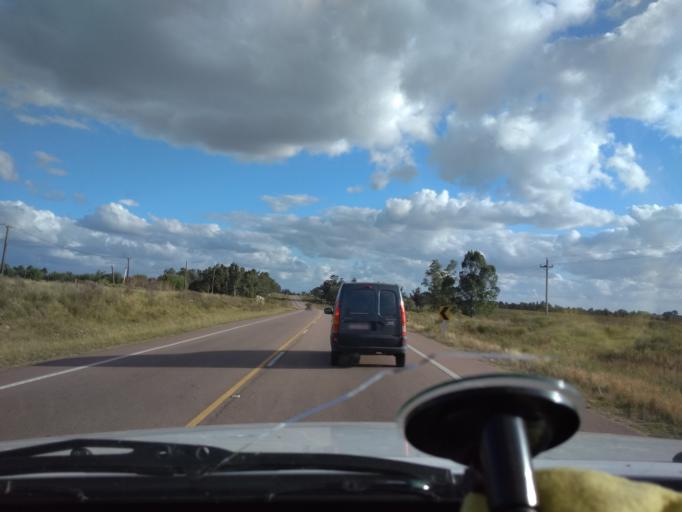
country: UY
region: Canelones
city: San Jacinto
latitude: -34.4683
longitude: -55.8302
